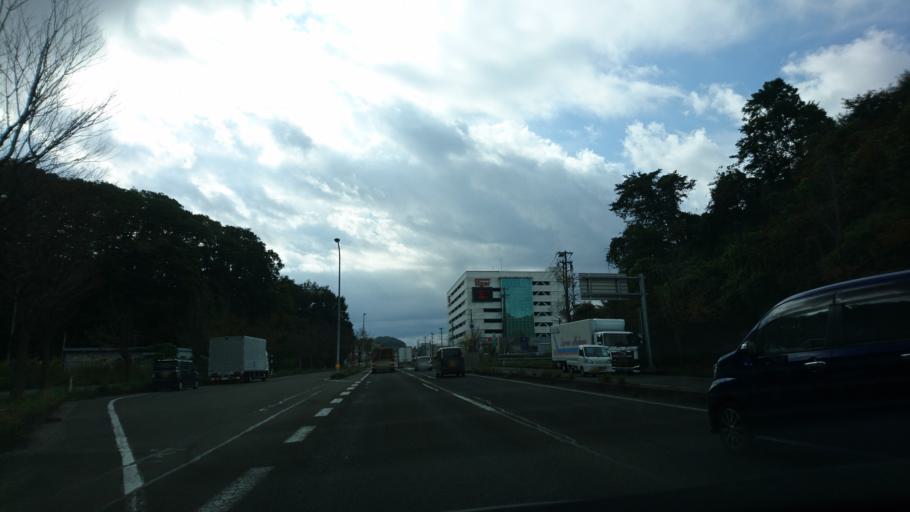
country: JP
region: Miyagi
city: Tomiya
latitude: 38.3727
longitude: 140.8741
